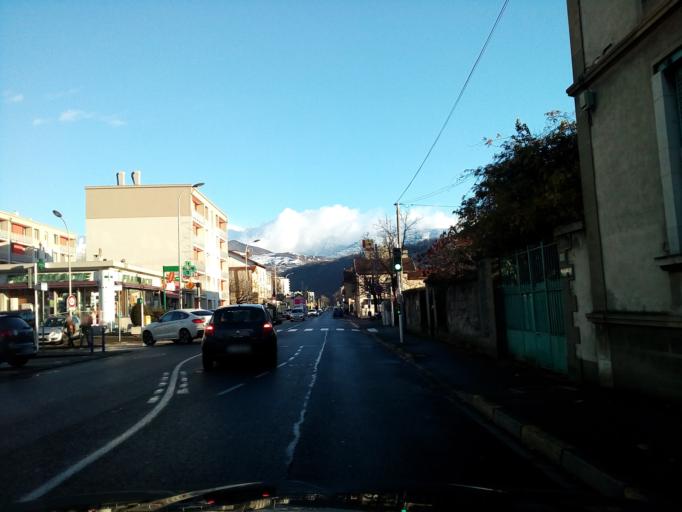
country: FR
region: Rhone-Alpes
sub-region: Departement de l'Isere
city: Saint-Martin-d'Heres
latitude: 45.1828
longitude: 5.7584
